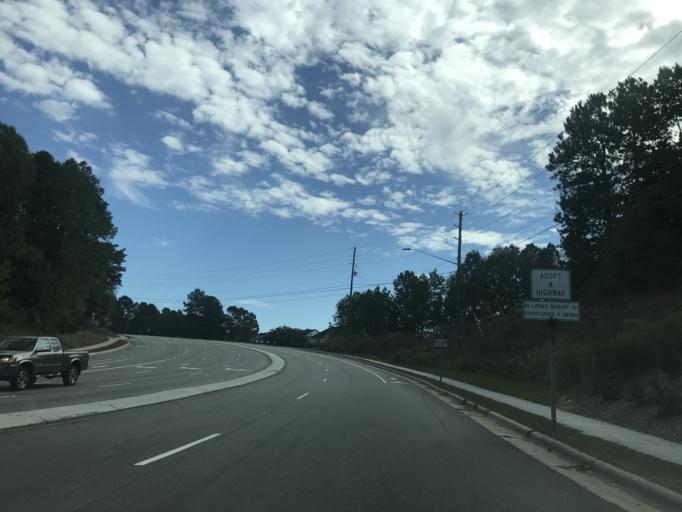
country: US
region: North Carolina
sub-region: Wake County
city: Rolesville
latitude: 35.8856
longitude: -78.5257
